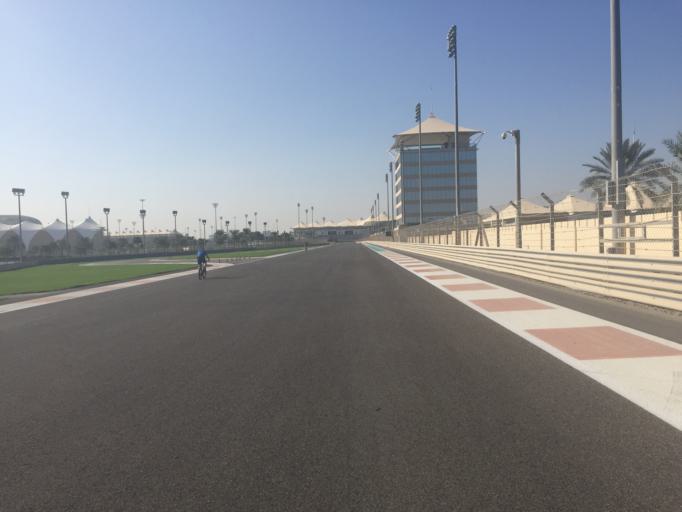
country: AE
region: Abu Dhabi
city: Abu Dhabi
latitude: 24.4745
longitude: 54.6037
